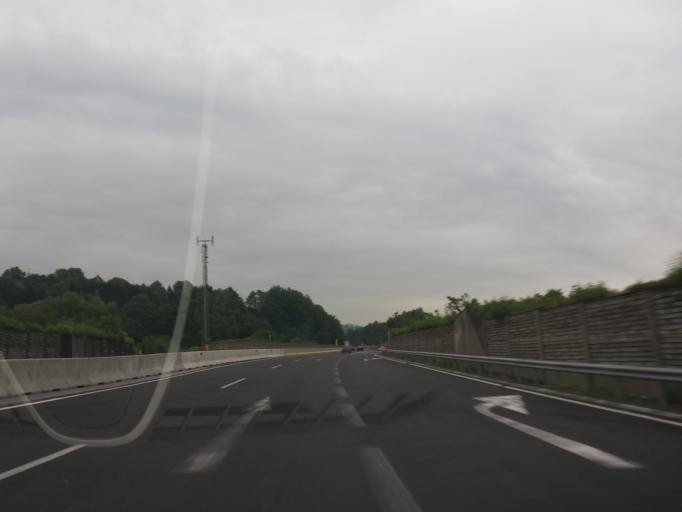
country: AT
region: Styria
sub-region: Politischer Bezirk Bruck-Muerzzuschlag
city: Kindberg
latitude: 47.5020
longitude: 15.4405
